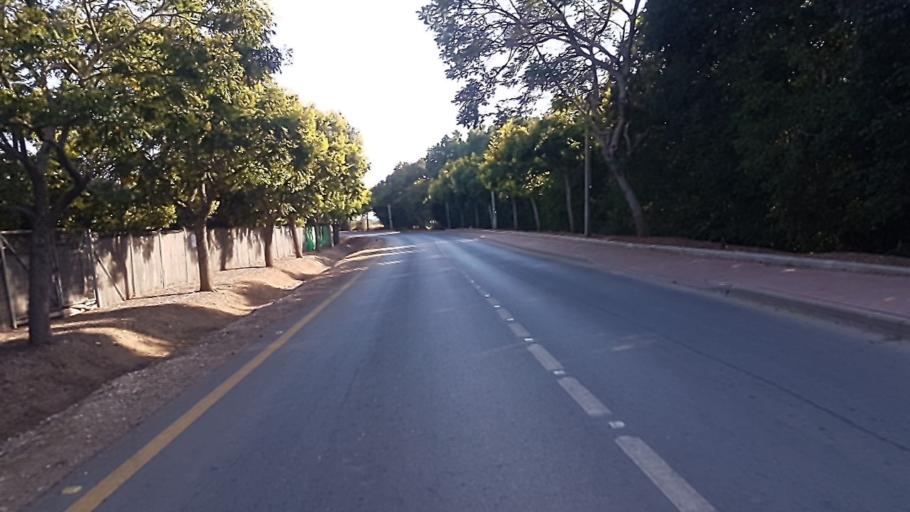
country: IL
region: Central District
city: Hod HaSharon
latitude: 32.1371
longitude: 34.9076
